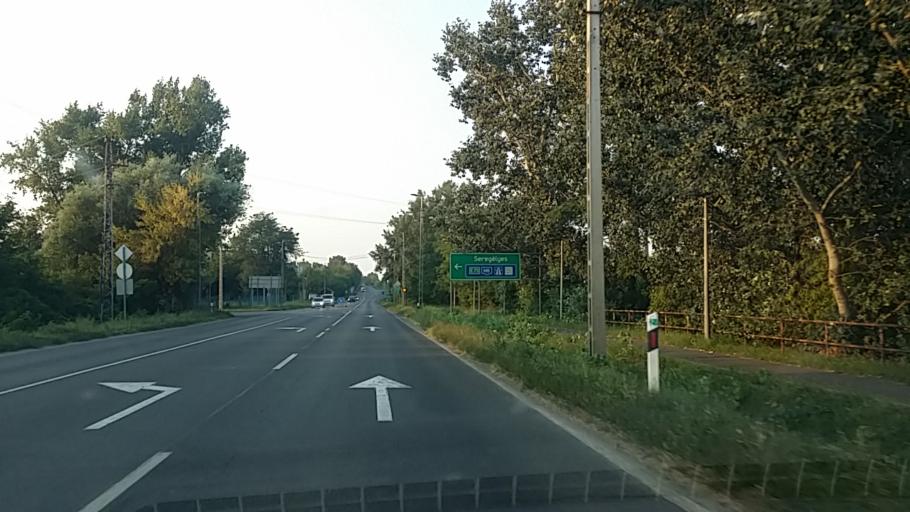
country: HU
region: Tolna
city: Dunafoldvar
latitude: 46.8300
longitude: 18.9080
